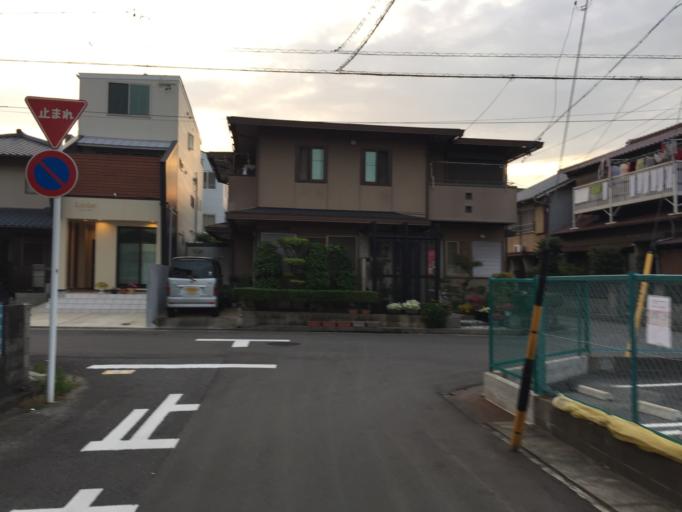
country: JP
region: Mie
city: Yokkaichi
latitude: 34.9615
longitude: 136.6258
